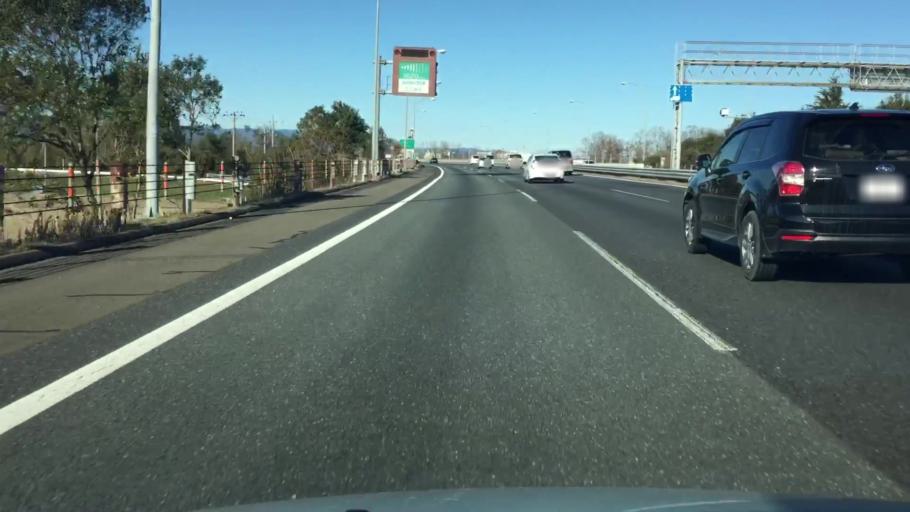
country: JP
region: Saitama
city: Kawagoe
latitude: 35.9094
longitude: 139.4461
